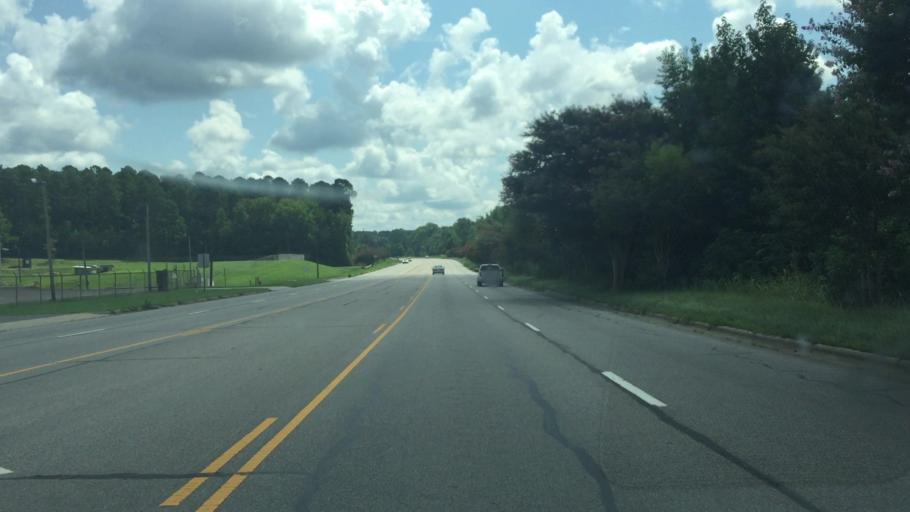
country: US
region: North Carolina
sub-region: Anson County
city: Wadesboro
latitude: 34.9635
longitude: -80.0440
